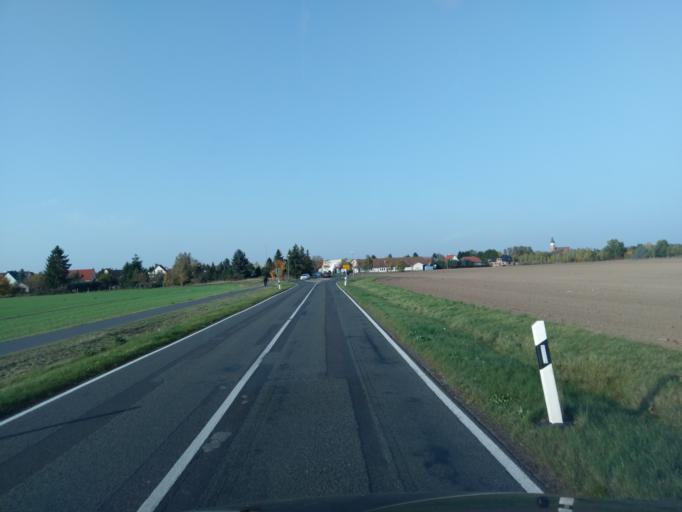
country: DE
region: Brandenburg
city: Herzberg
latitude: 51.6804
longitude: 13.2298
